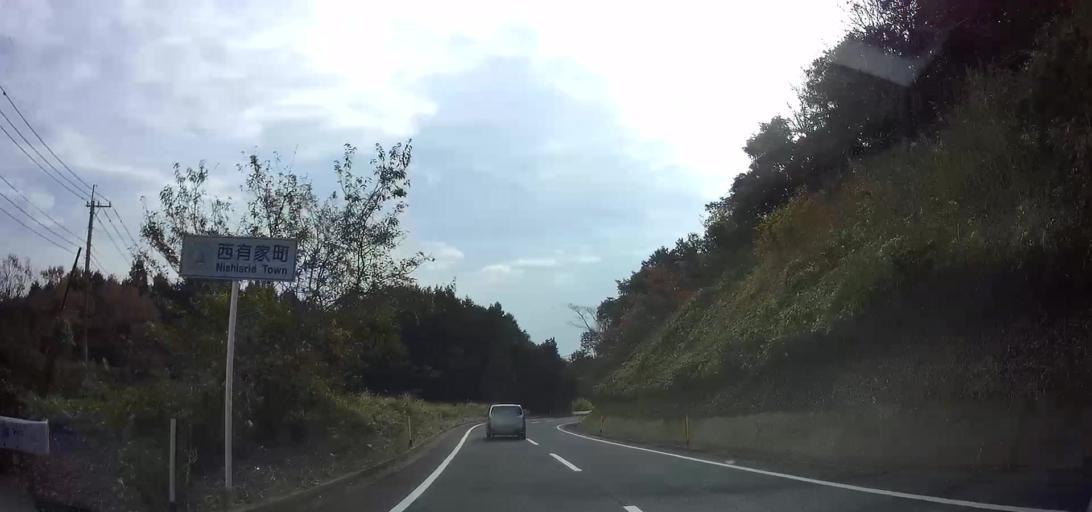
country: JP
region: Nagasaki
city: Shimabara
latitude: 32.6949
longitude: 130.2539
